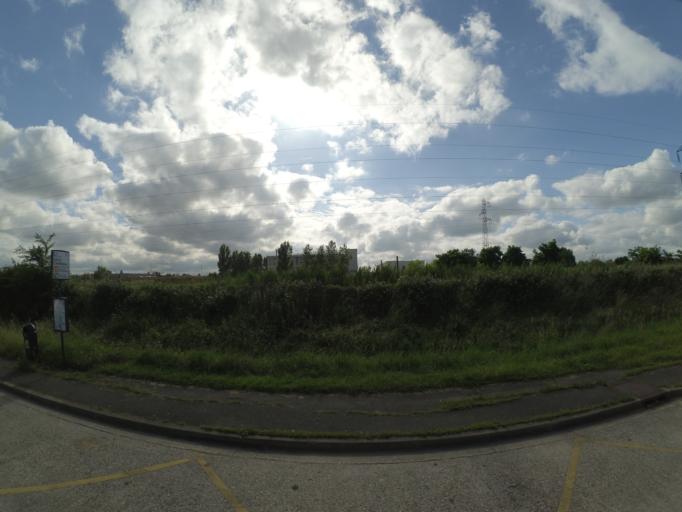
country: FR
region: Aquitaine
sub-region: Departement de la Gironde
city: Lormont
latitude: 44.8869
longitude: -0.5493
